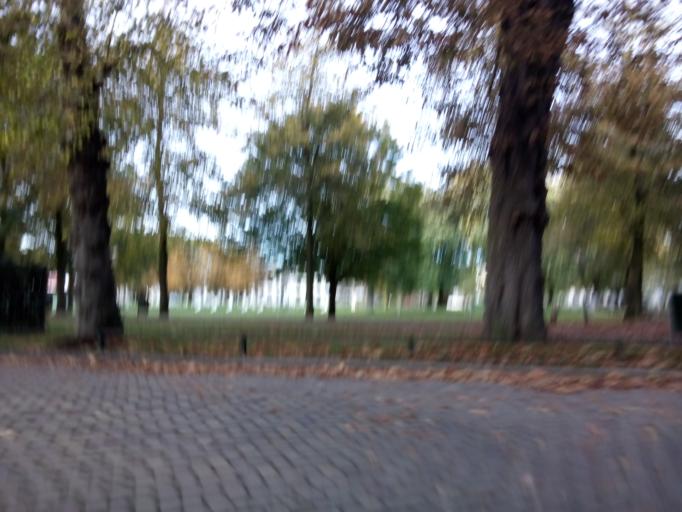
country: NL
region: Utrecht
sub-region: Gemeente Utrecht
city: Utrecht
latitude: 52.0887
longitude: 5.1283
